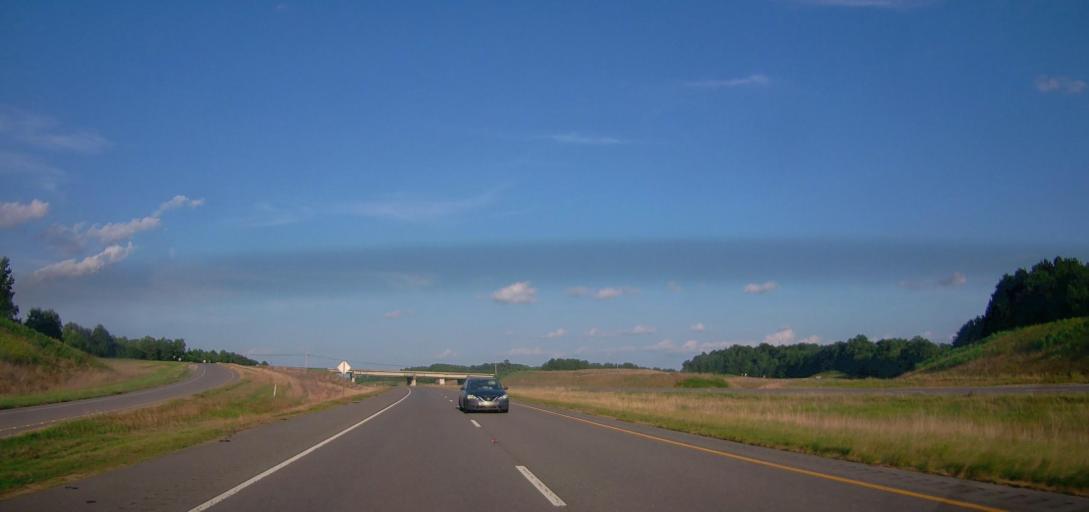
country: US
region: Alabama
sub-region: Walker County
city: Jasper
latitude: 33.8077
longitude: -87.2834
